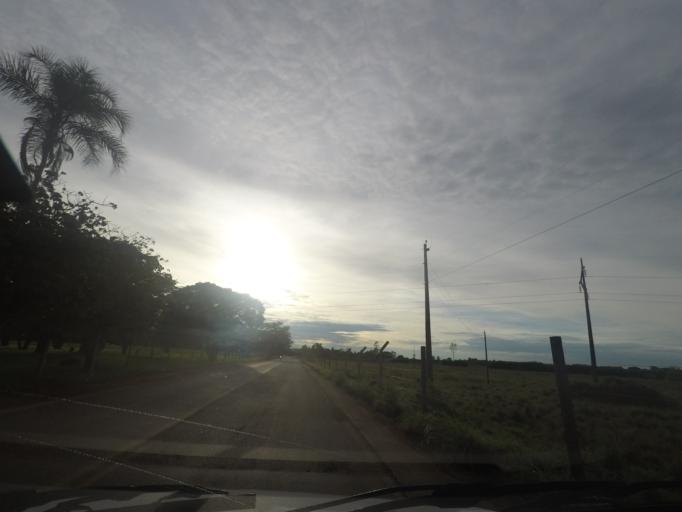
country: BR
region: Goias
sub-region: Trindade
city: Trindade
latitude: -16.7337
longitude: -49.4208
